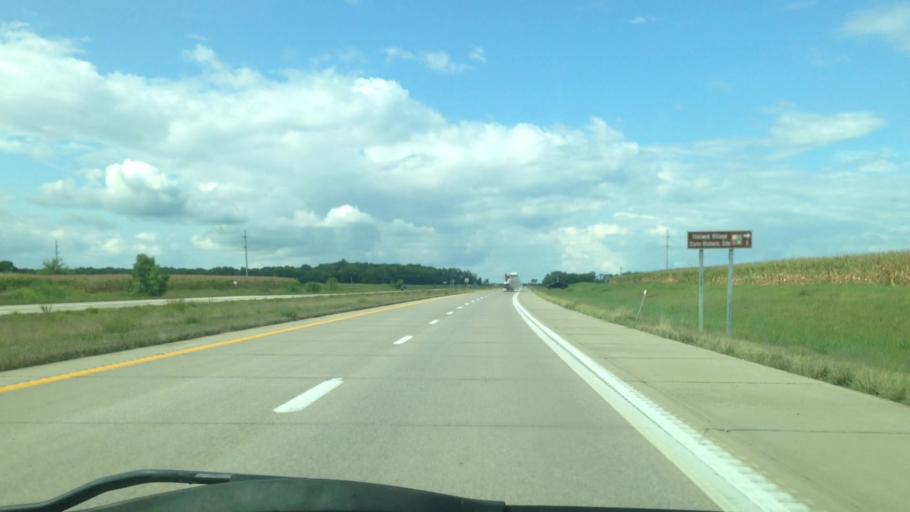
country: US
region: Missouri
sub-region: Clark County
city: Kahoka
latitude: 40.4211
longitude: -91.5722
